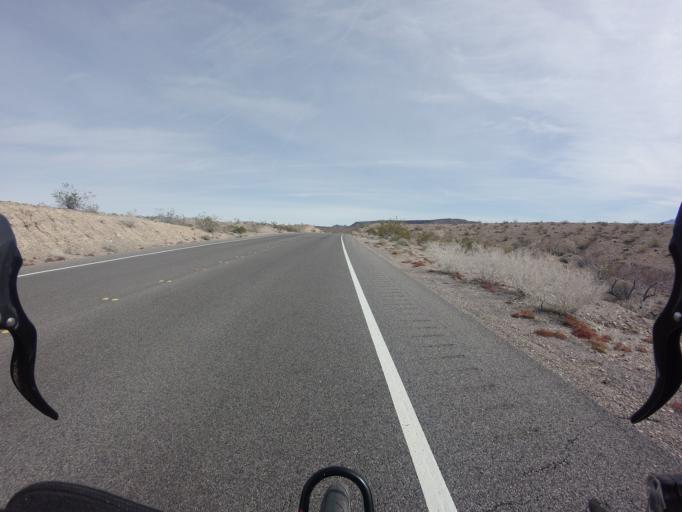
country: US
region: Nevada
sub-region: Clark County
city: Boulder City
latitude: 36.1571
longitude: -114.8152
